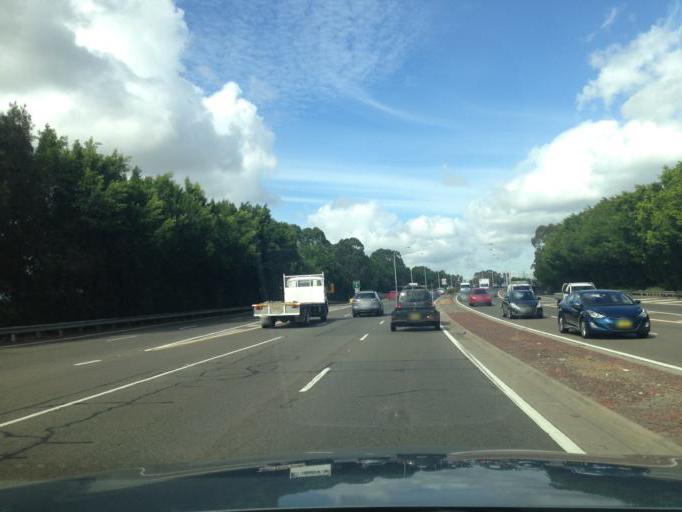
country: AU
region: New South Wales
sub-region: Canada Bay
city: Concord West
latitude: -33.8517
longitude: 151.0801
